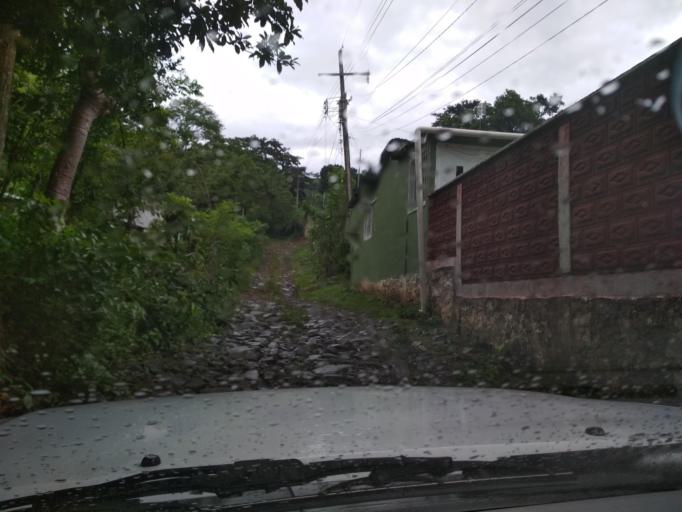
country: MX
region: Veracruz
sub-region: San Andres Tuxtla
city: San Isidro Xoteapan (San Isidro Texcaltitan)
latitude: 18.4628
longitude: -95.2357
